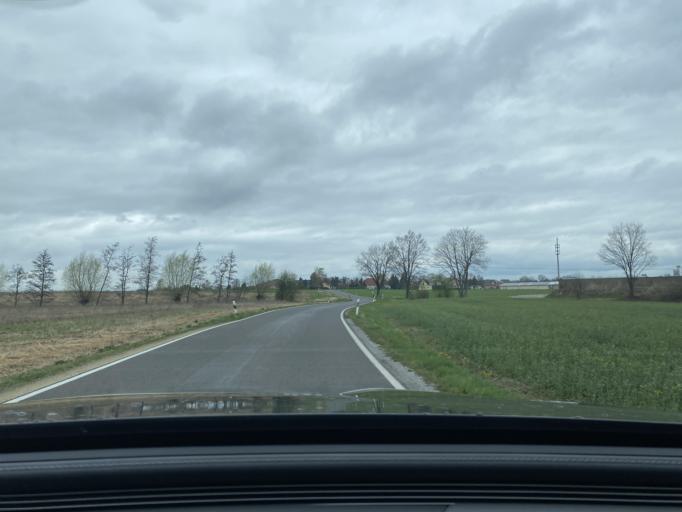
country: DE
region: Saxony
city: Neschwitz
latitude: 51.2603
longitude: 14.3315
